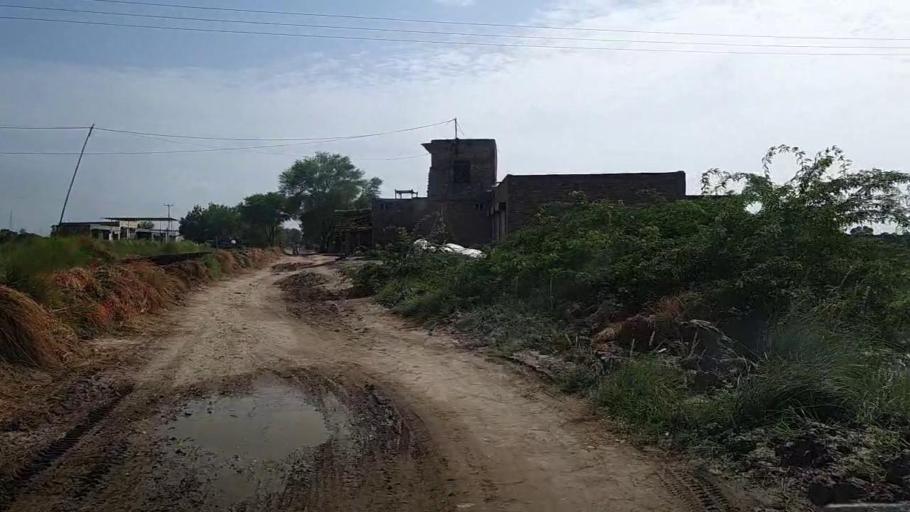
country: PK
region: Sindh
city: Bhiria
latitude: 26.8792
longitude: 68.2308
